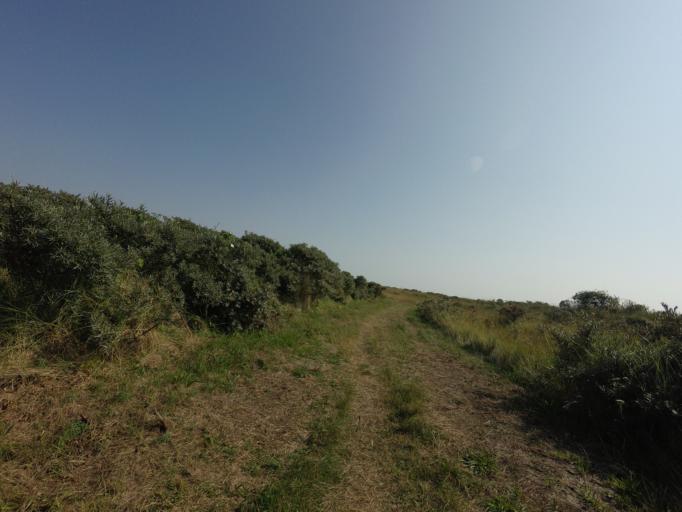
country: NL
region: Friesland
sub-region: Gemeente Schiermonnikoog
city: Schiermonnikoog
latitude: 53.4960
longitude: 6.2421
